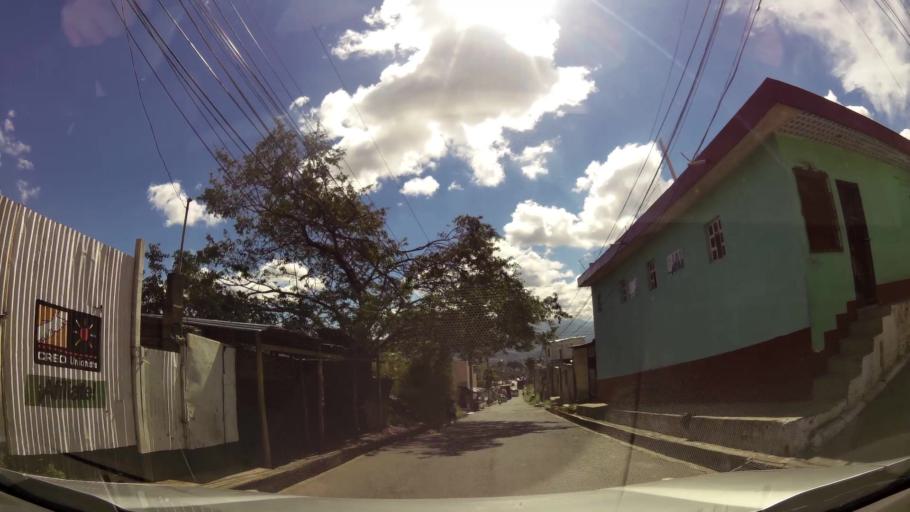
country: GT
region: Guatemala
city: Petapa
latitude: 14.5460
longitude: -90.5459
